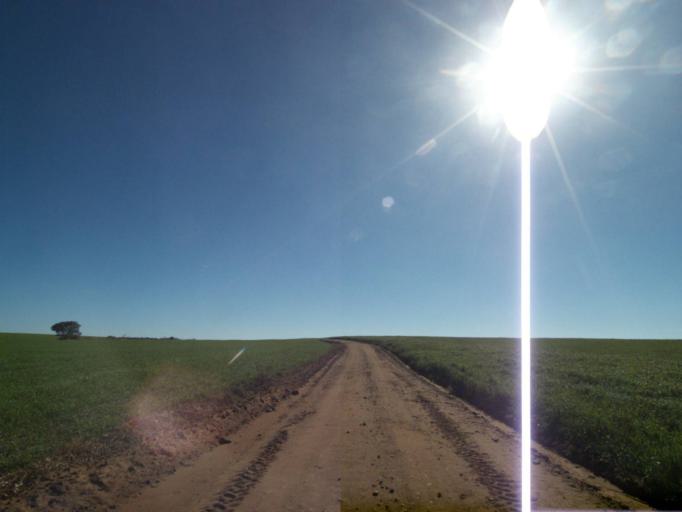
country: BR
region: Parana
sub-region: Tibagi
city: Tibagi
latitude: -24.5758
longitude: -50.2655
